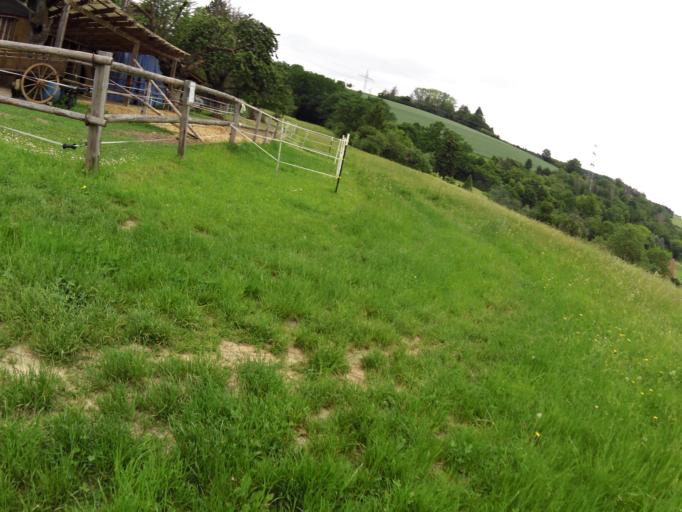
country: DE
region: Bavaria
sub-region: Regierungsbezirk Unterfranken
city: Zell am Main
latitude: 49.8141
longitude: 9.8620
